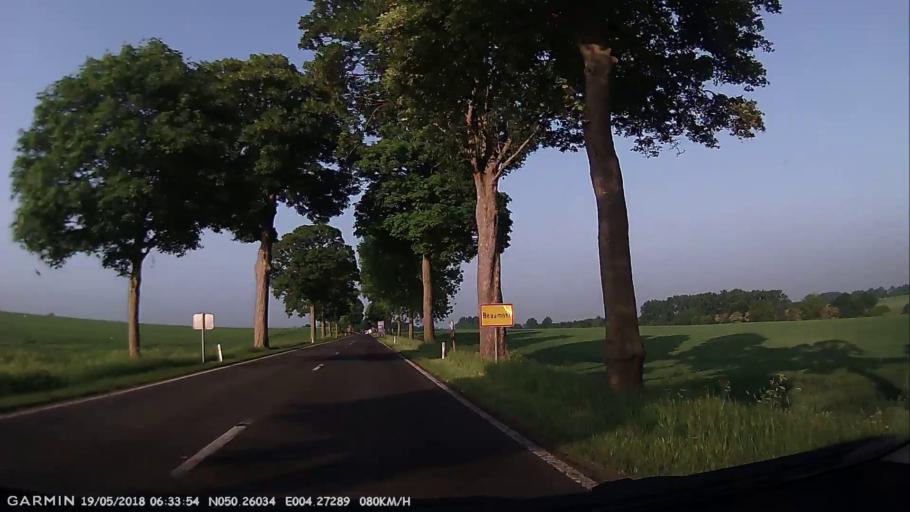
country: BE
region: Wallonia
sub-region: Province du Hainaut
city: Beaumont
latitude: 50.2602
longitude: 4.2728
